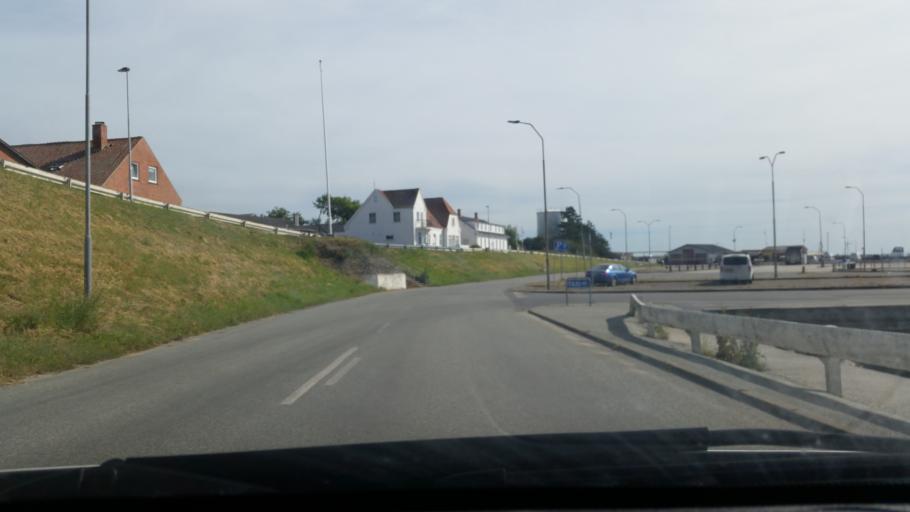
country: DK
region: Central Jutland
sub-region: Samso Kommune
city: Tranebjerg
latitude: 55.7965
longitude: 10.5307
